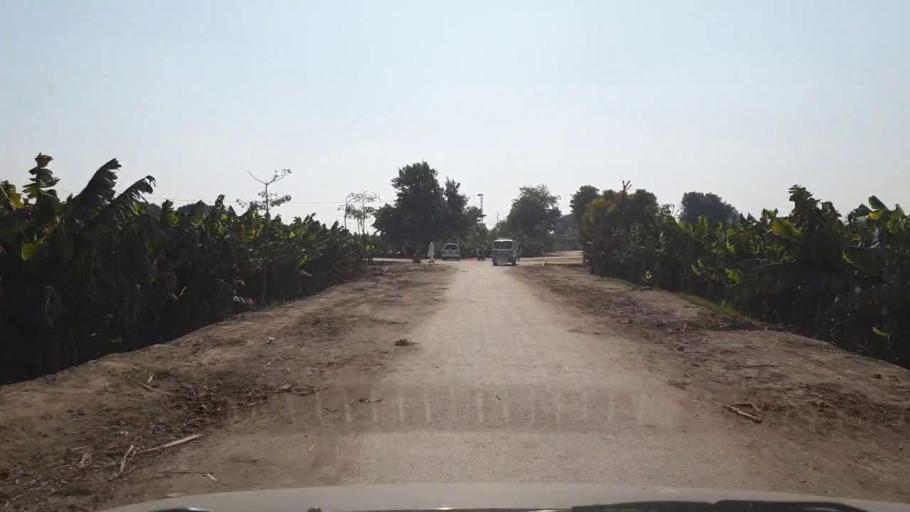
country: PK
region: Sindh
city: Tando Jam
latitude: 25.4153
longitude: 68.6323
